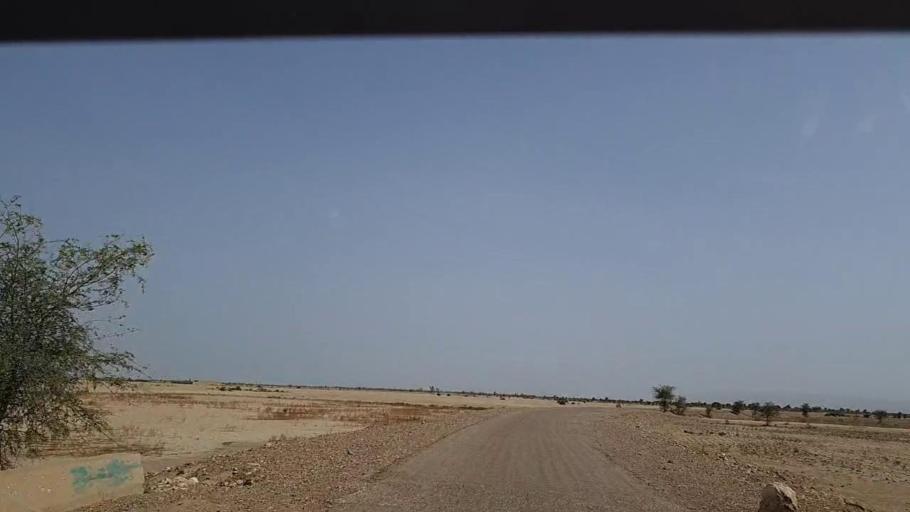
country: PK
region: Sindh
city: Johi
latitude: 26.6679
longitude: 67.5087
